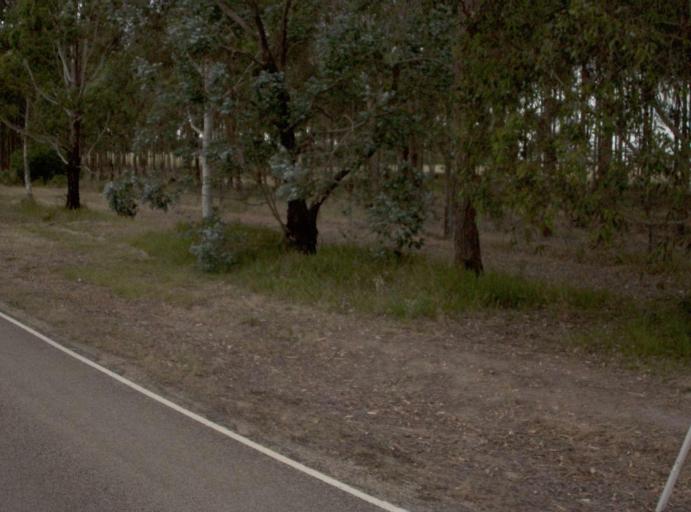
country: AU
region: Victoria
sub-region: Wellington
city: Sale
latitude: -38.0035
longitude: 147.2607
